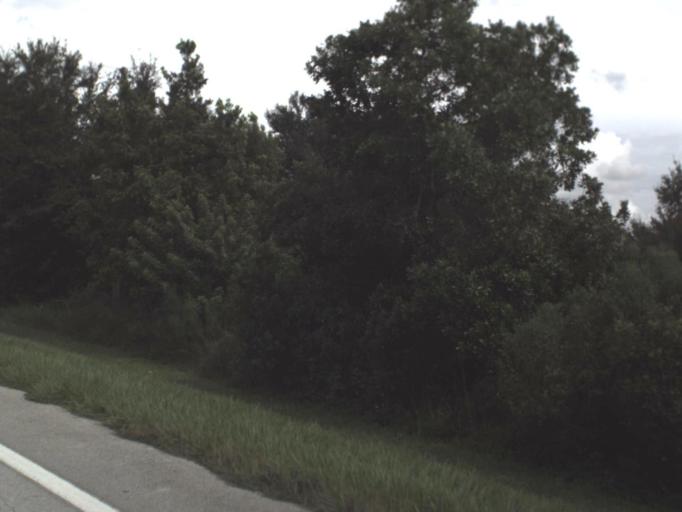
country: US
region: Florida
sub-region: DeSoto County
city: Nocatee
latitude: 27.2019
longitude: -81.9298
